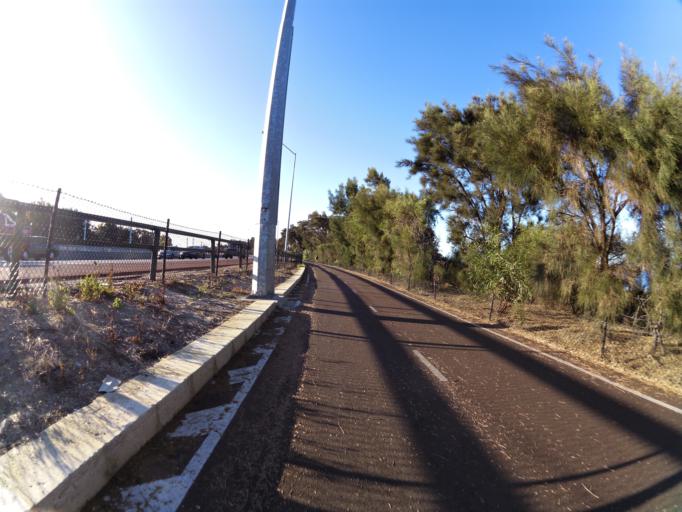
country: AU
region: Western Australia
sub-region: South Perth
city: South Perth
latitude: -31.9787
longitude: 115.8480
